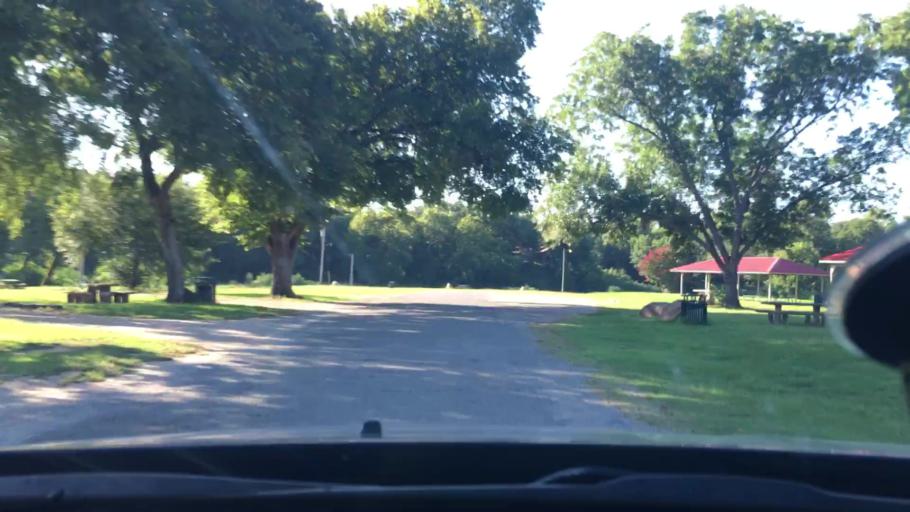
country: US
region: Oklahoma
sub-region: Johnston County
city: Tishomingo
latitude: 34.2340
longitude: -96.6832
